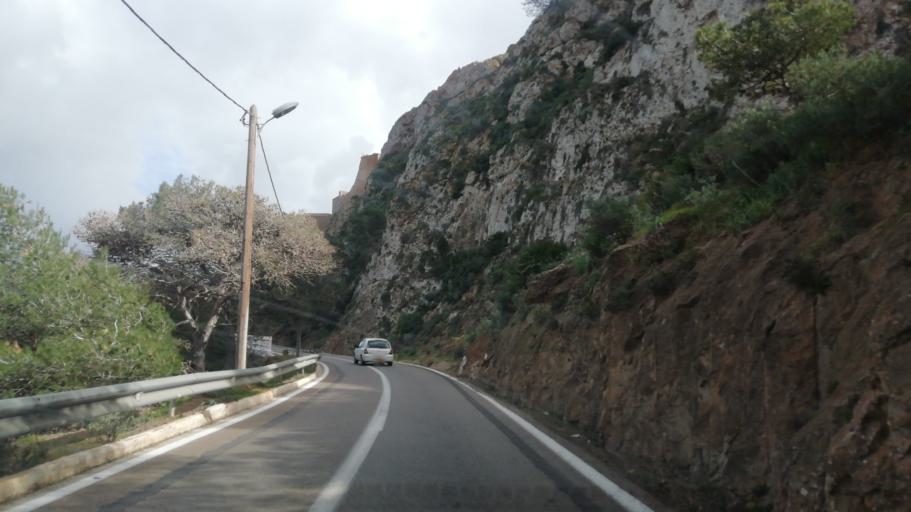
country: DZ
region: Oran
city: Oran
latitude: 35.7091
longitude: -0.6683
